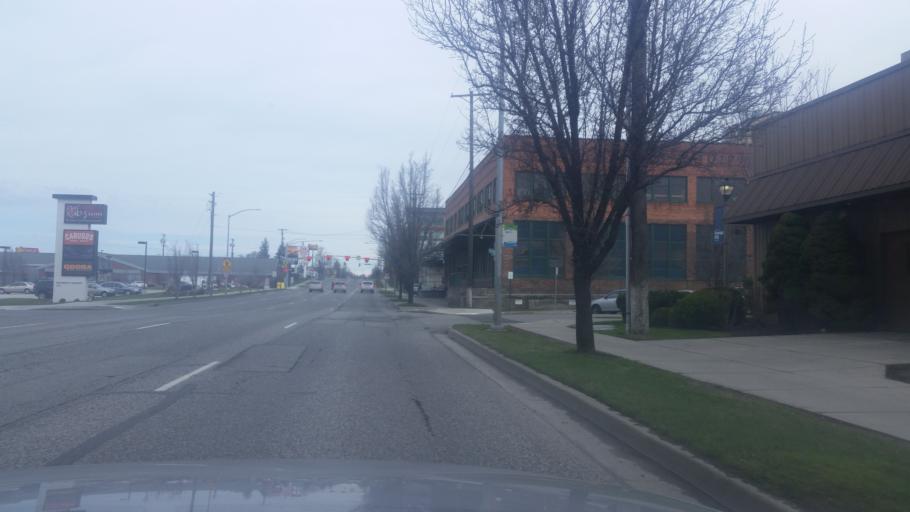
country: US
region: Washington
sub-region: Spokane County
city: Spokane
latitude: 47.6669
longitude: -117.4094
